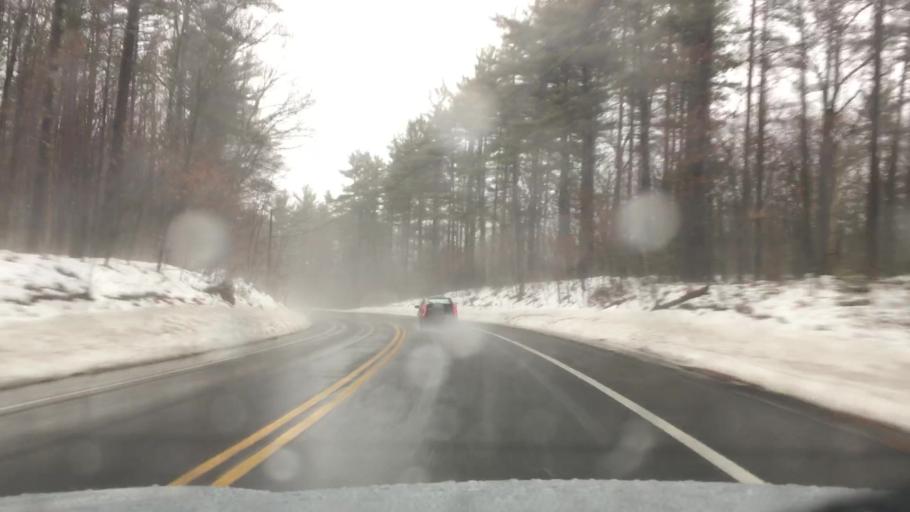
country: US
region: Massachusetts
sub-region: Franklin County
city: Wendell
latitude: 42.5072
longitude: -72.3285
